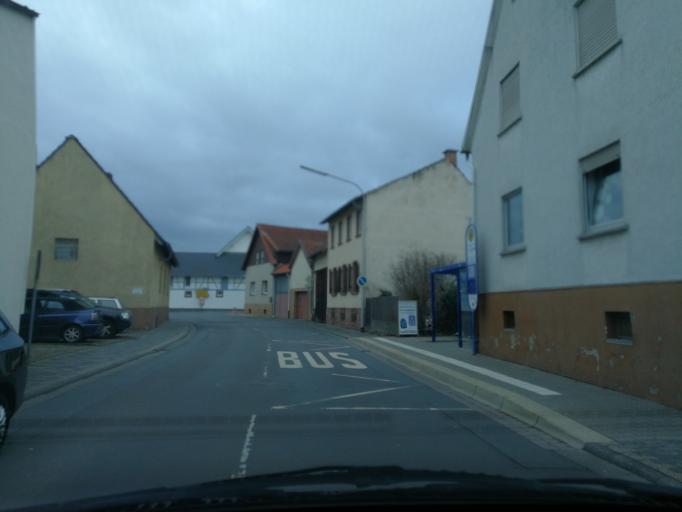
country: DE
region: Hesse
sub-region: Regierungsbezirk Darmstadt
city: Rossdorf
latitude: 49.8440
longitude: 8.7931
